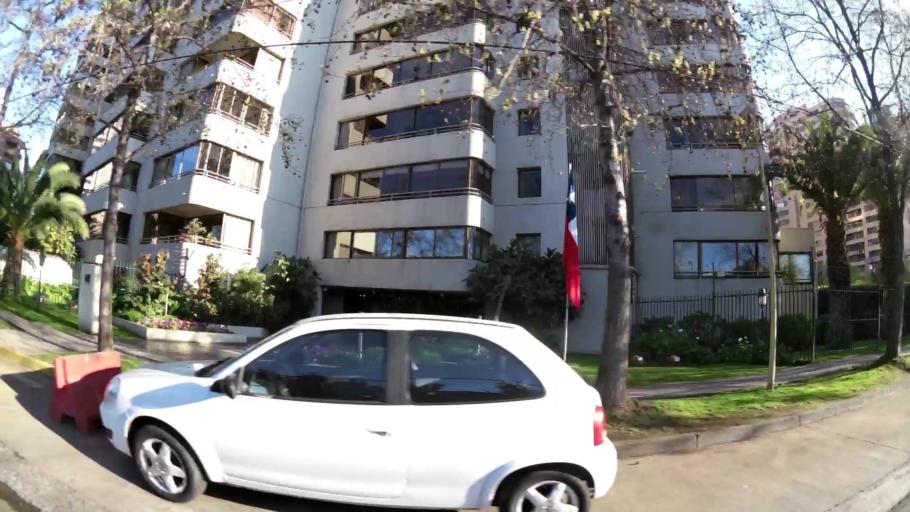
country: CL
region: Santiago Metropolitan
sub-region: Provincia de Santiago
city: Villa Presidente Frei, Nunoa, Santiago, Chile
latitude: -33.4062
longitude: -70.5844
